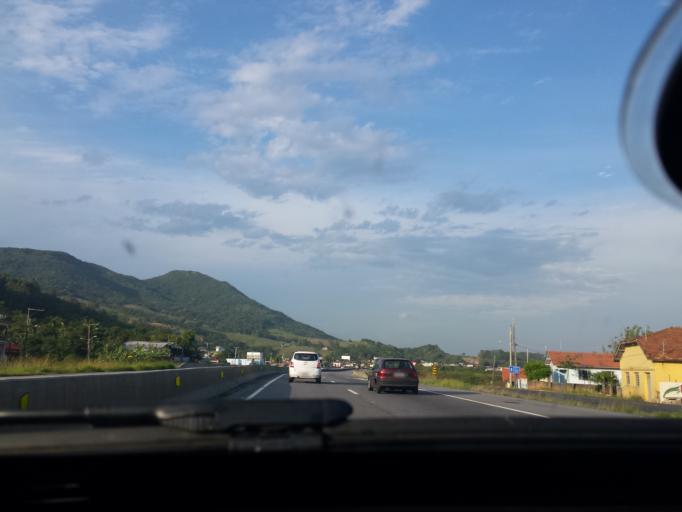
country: BR
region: Santa Catarina
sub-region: Laguna
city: Laguna
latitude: -28.4275
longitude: -48.8661
